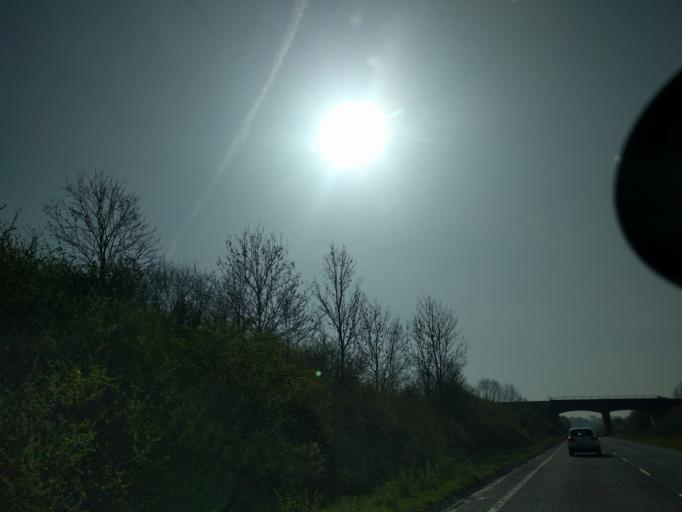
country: GB
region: England
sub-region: Wiltshire
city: Chippenham
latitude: 51.4404
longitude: -2.1411
